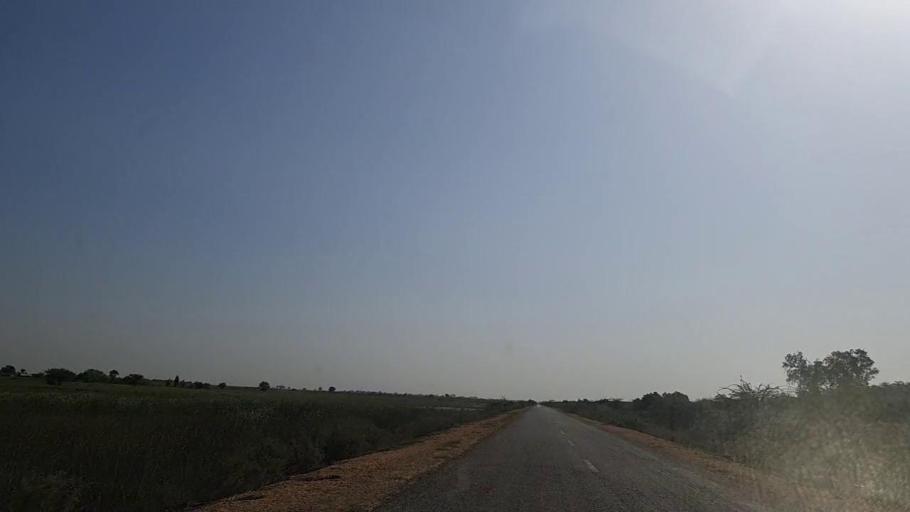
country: PK
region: Sindh
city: Jati
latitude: 24.4497
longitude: 68.2633
